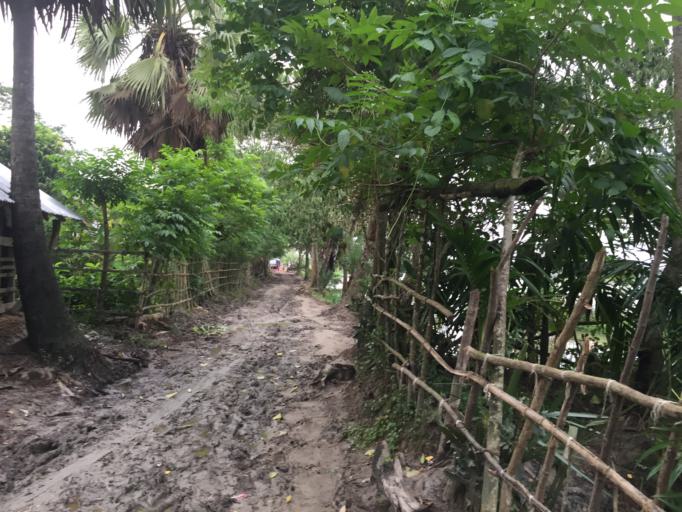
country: BD
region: Barisal
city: Mathba
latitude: 22.1921
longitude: 89.9311
